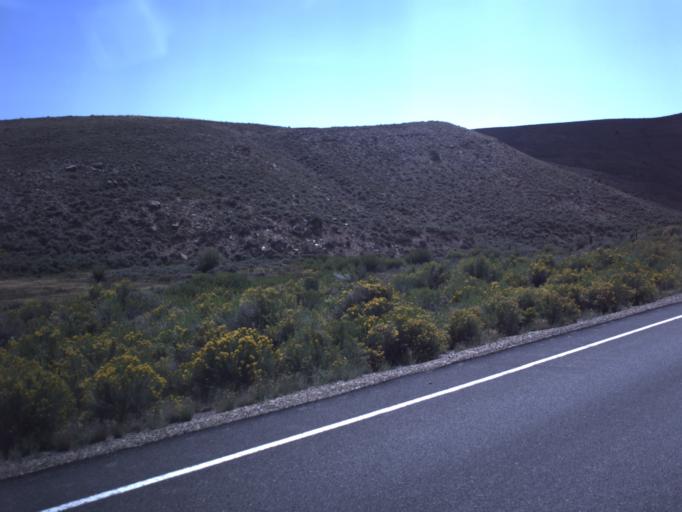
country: US
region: Utah
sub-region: Carbon County
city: Helper
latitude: 39.7968
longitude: -110.7846
